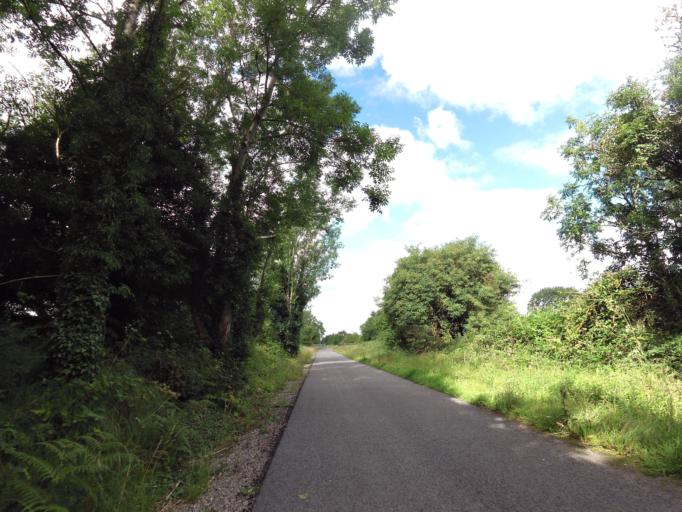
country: IE
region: Leinster
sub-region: An Iarmhi
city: Kilbeggan
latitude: 53.4562
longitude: -7.5197
